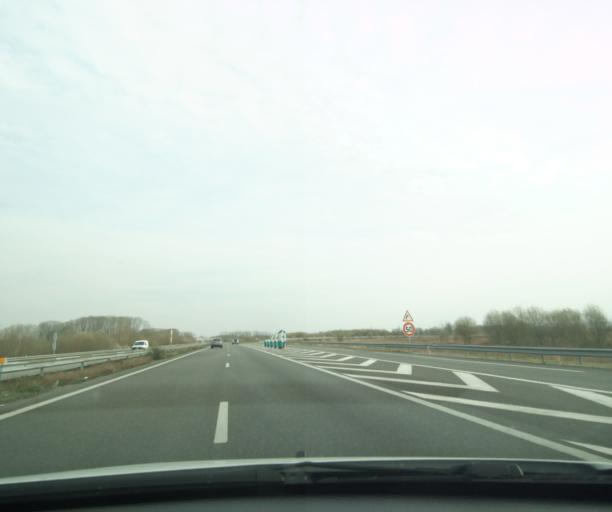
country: FR
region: Aquitaine
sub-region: Departement des Pyrenees-Atlantiques
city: Poey-de-Lescar
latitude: 43.3530
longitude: -0.4459
